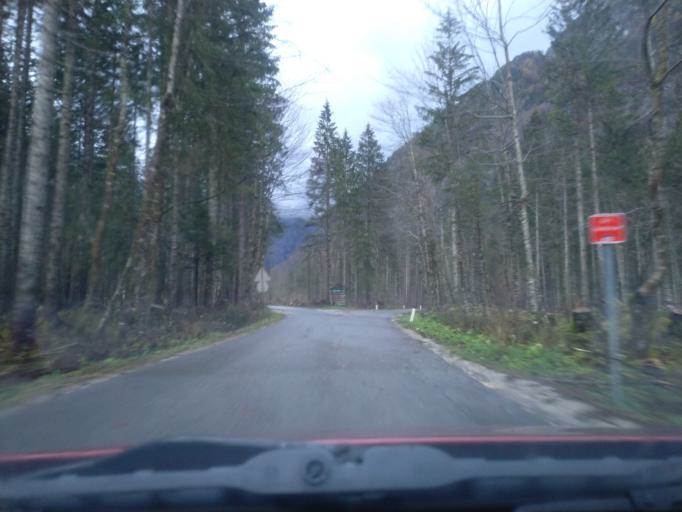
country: SI
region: Solcava
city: Solcava
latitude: 46.4015
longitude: 14.6319
